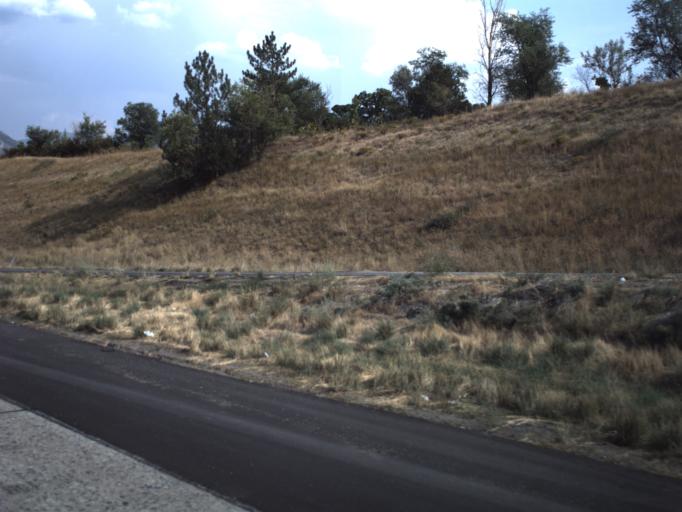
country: US
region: Utah
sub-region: Salt Lake County
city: Willard
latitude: 40.7196
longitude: -111.8520
